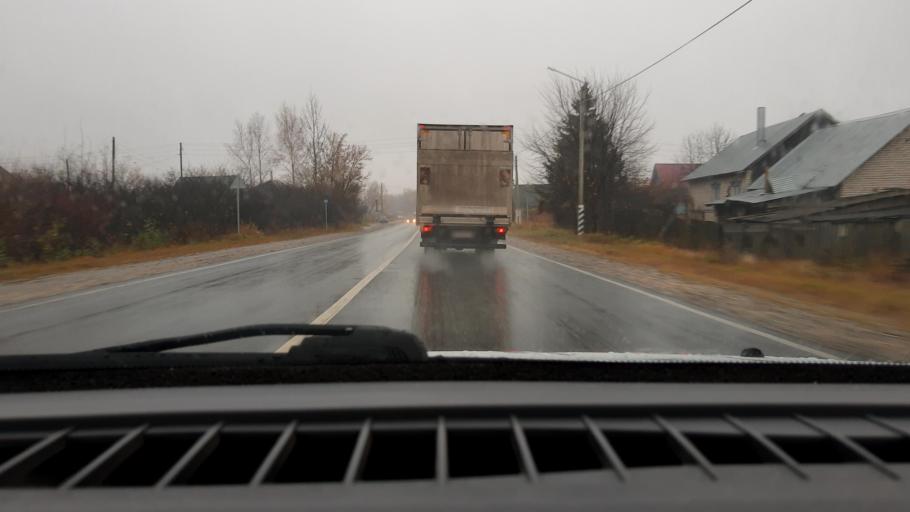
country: RU
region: Nizjnij Novgorod
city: Linda
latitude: 56.5667
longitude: 44.0248
